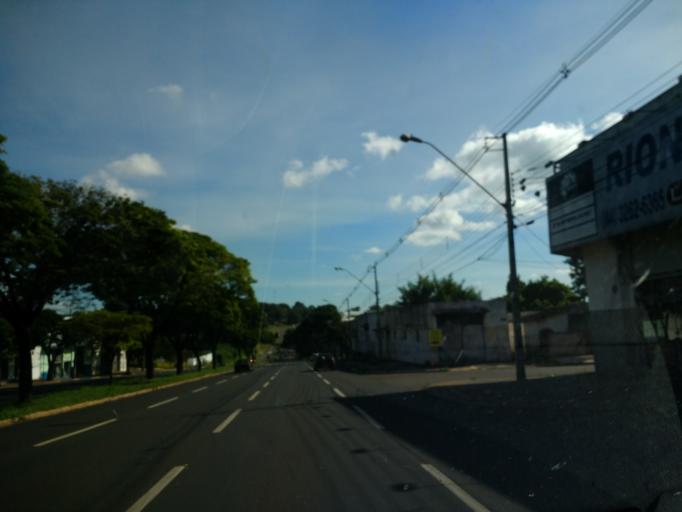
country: BR
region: Parana
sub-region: Maringa
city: Maringa
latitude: -23.4172
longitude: -51.9589
